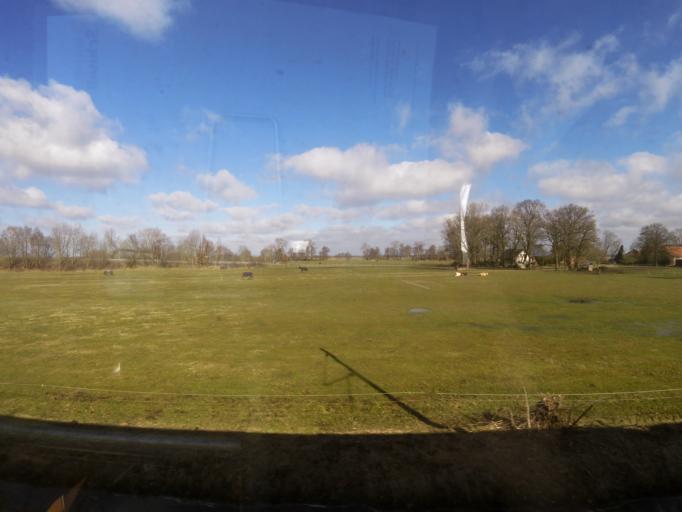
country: DE
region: Lower Saxony
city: Oyten
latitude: 53.0839
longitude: 8.9739
